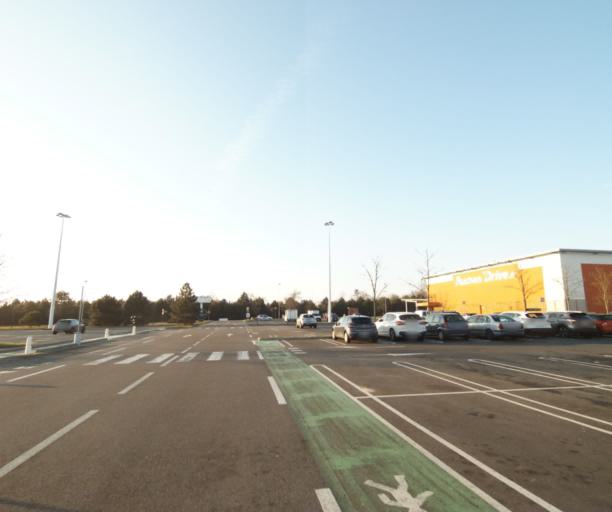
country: FR
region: Lorraine
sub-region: Departement de Meurthe-et-Moselle
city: Laxou
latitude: 48.6908
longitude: 6.1270
